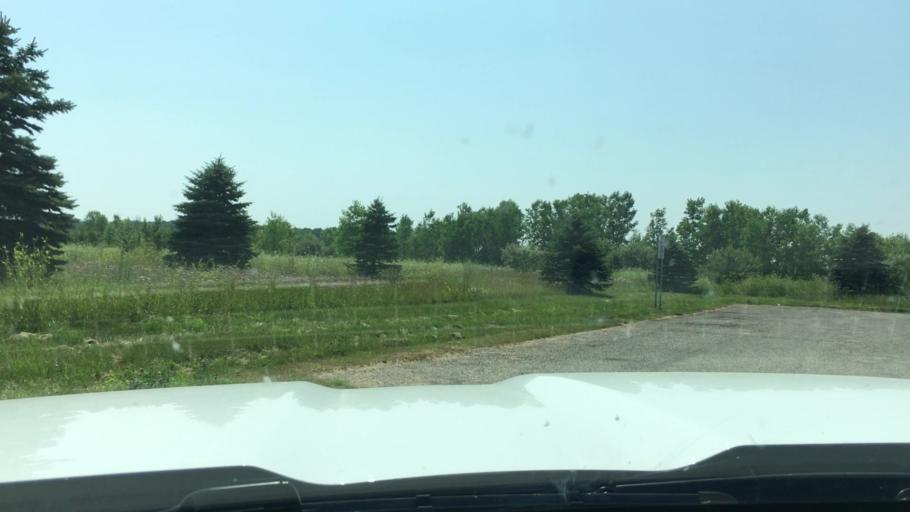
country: US
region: Michigan
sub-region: Gratiot County
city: Ithaca
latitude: 43.1747
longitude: -84.5587
